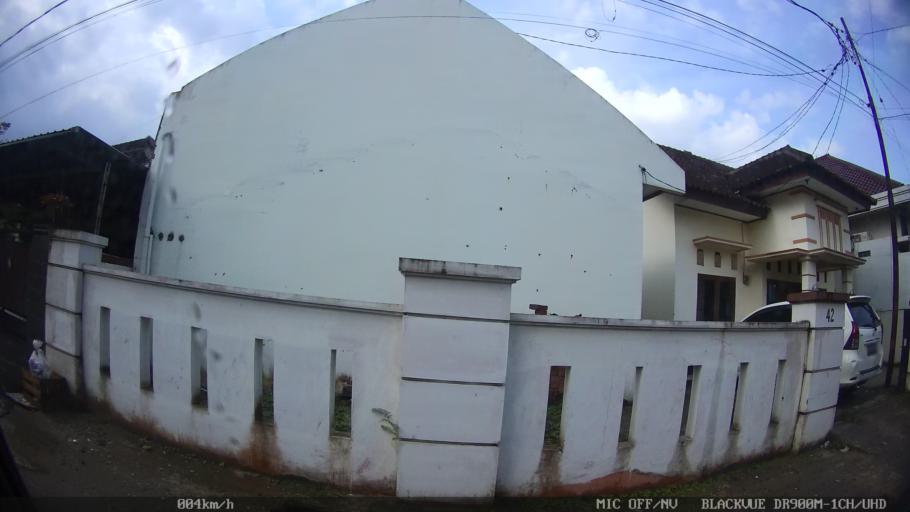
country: ID
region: Lampung
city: Kedaton
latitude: -5.3889
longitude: 105.2966
